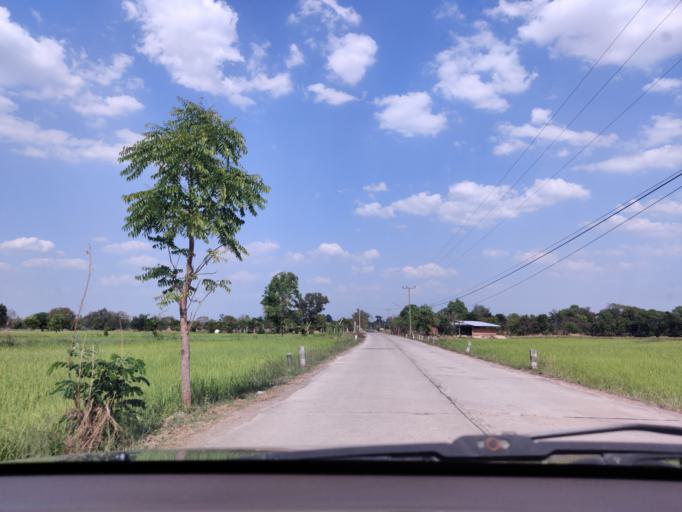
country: TH
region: Sisaket
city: Si Sa Ket
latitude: 15.0662
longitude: 104.3560
